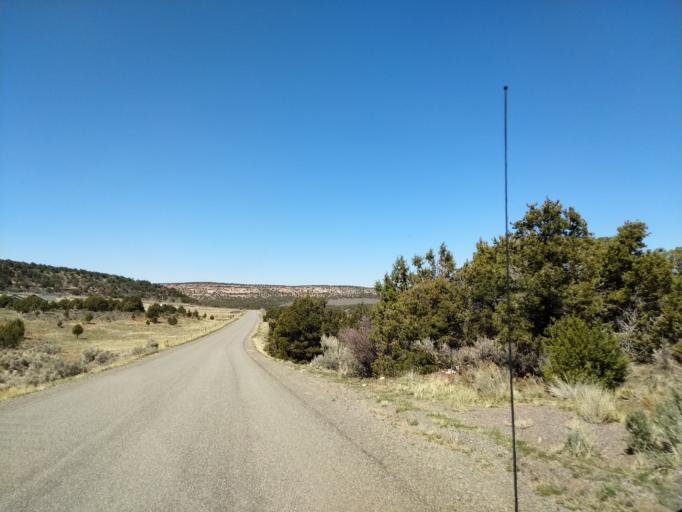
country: US
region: Colorado
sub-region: Mesa County
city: Loma
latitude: 38.9558
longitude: -108.9994
